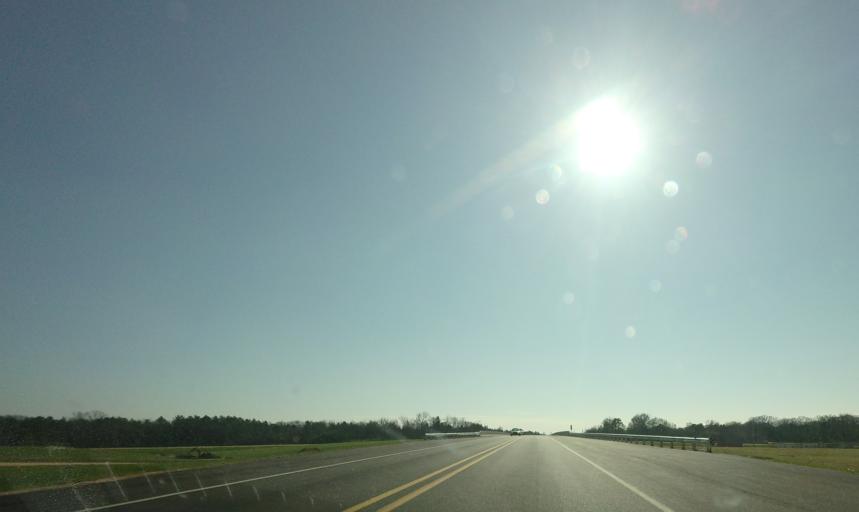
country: US
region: Mississippi
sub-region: Marshall County
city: Byhalia
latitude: 34.8960
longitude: -89.6892
